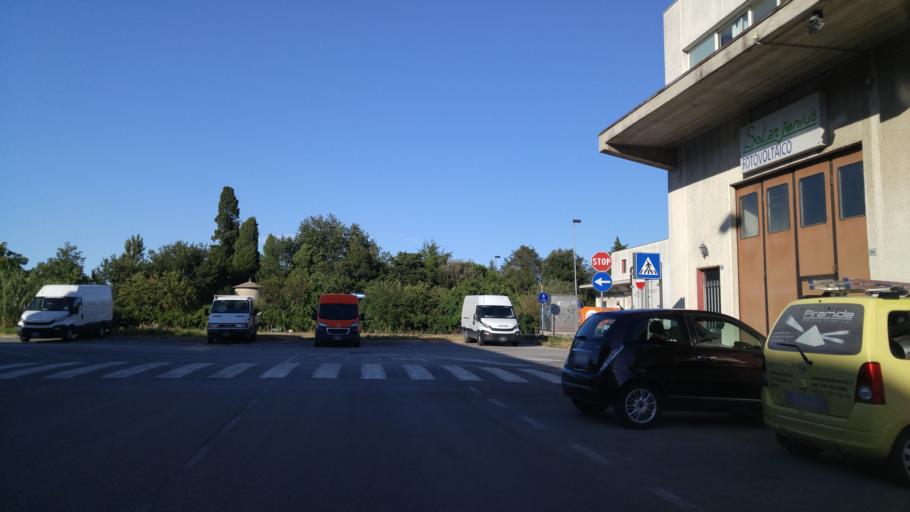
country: IT
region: The Marches
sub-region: Provincia di Pesaro e Urbino
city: Pesaro
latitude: 43.8870
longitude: 12.8776
